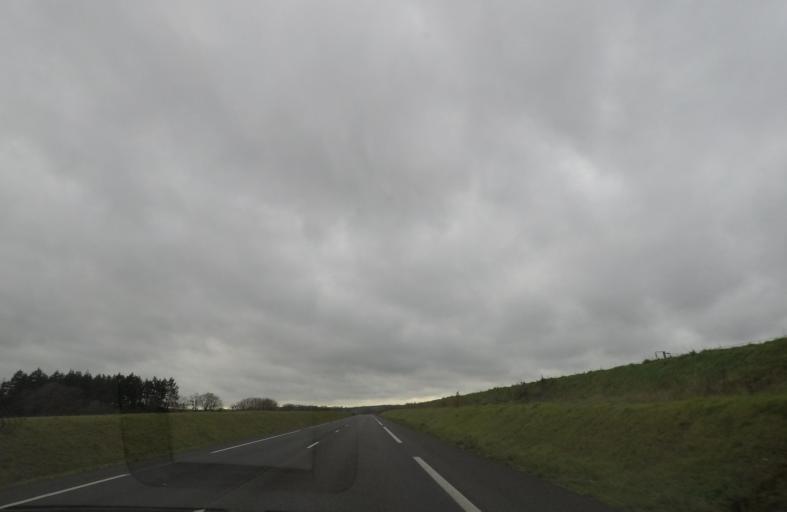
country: FR
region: Centre
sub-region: Departement du Loir-et-Cher
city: Villiers-sur-Loir
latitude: 47.7908
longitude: 1.0076
